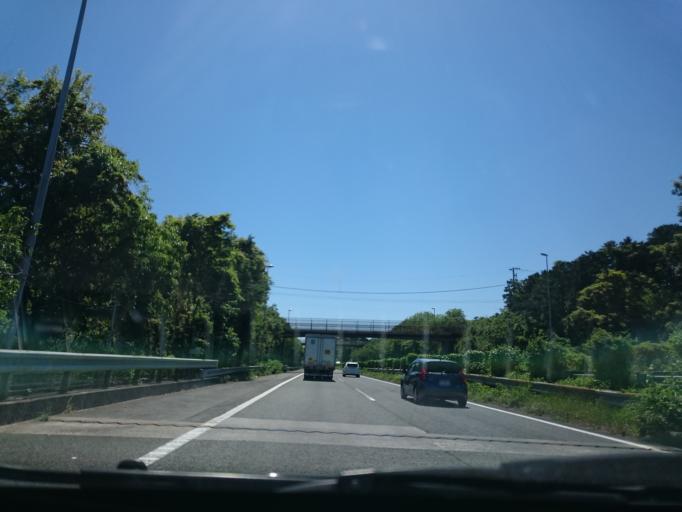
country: JP
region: Shizuoka
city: Mishima
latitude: 35.1683
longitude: 138.8937
